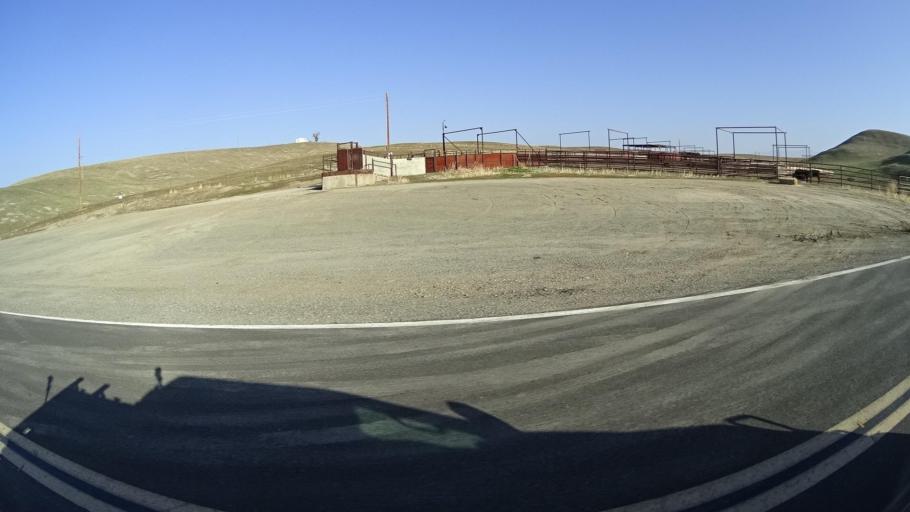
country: US
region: California
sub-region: Tulare County
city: Richgrove
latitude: 35.7463
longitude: -118.9326
